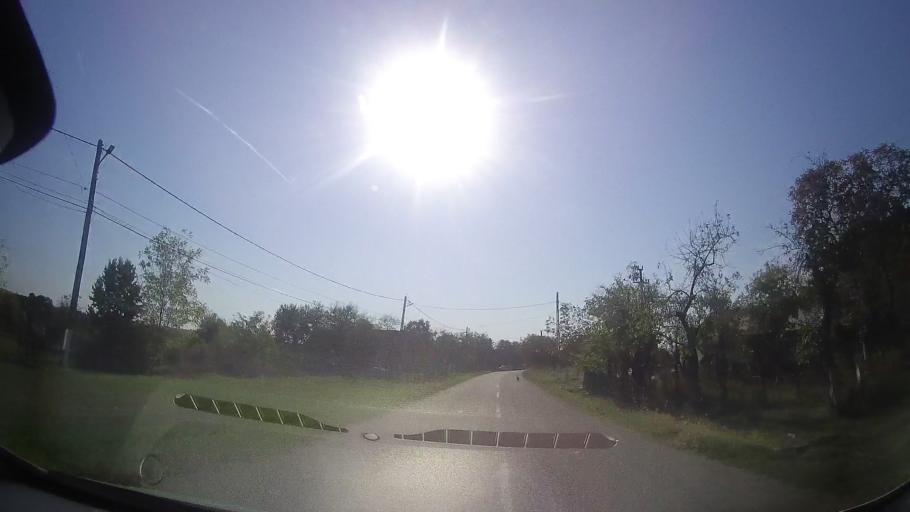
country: RO
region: Timis
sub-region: Comuna Topolovatu Mare
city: Topolovatu Mare
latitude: 45.8185
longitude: 21.5787
